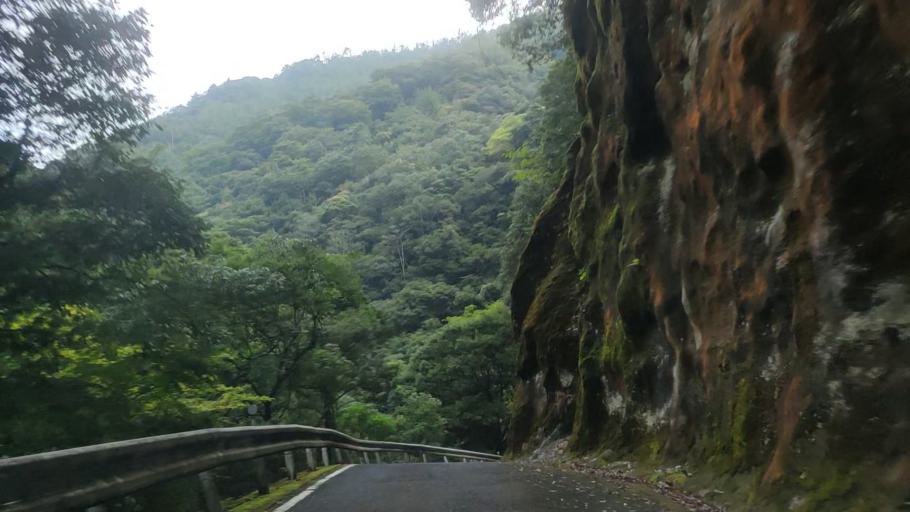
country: JP
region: Wakayama
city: Koya
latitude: 34.2495
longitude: 135.6535
